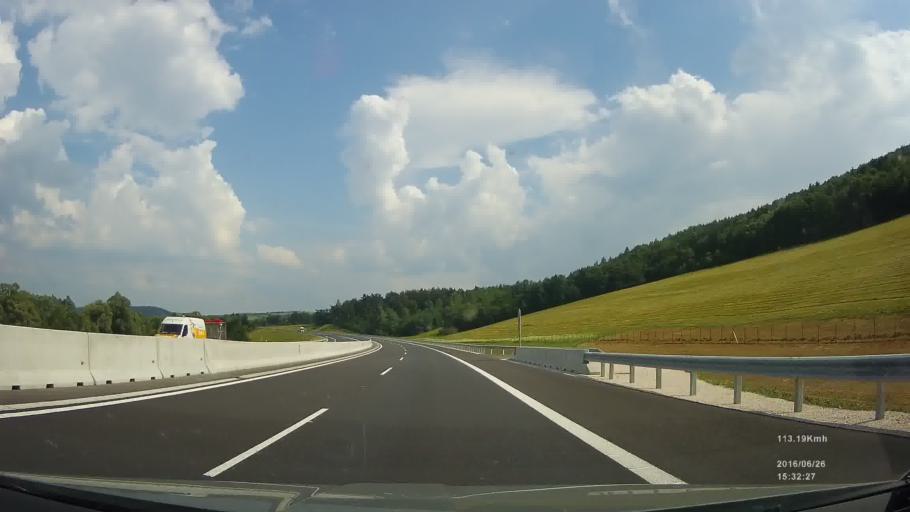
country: SK
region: Presovsky
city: Sabinov
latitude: 49.0138
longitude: 21.0410
